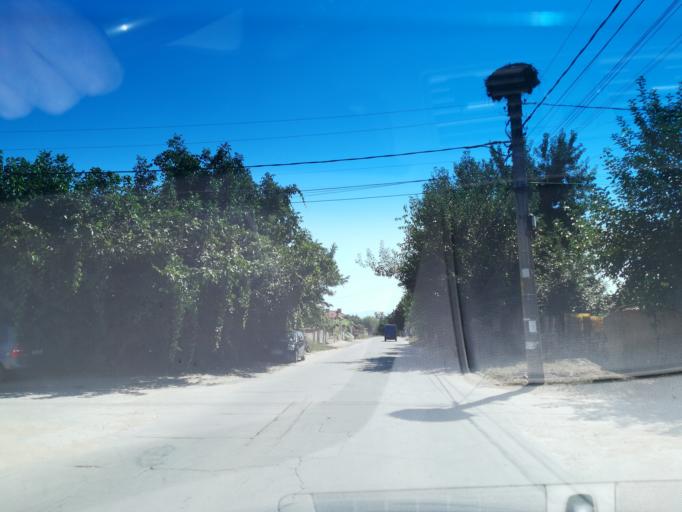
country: BG
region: Pazardzhik
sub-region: Obshtina Pazardzhik
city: Pazardzhik
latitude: 42.2774
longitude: 24.3957
